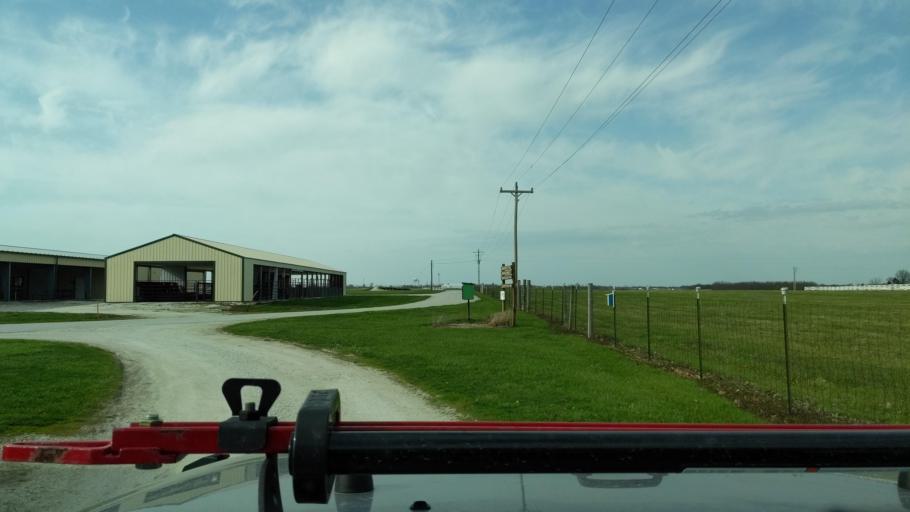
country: US
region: Missouri
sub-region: Macon County
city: Macon
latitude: 39.7210
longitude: -92.4597
